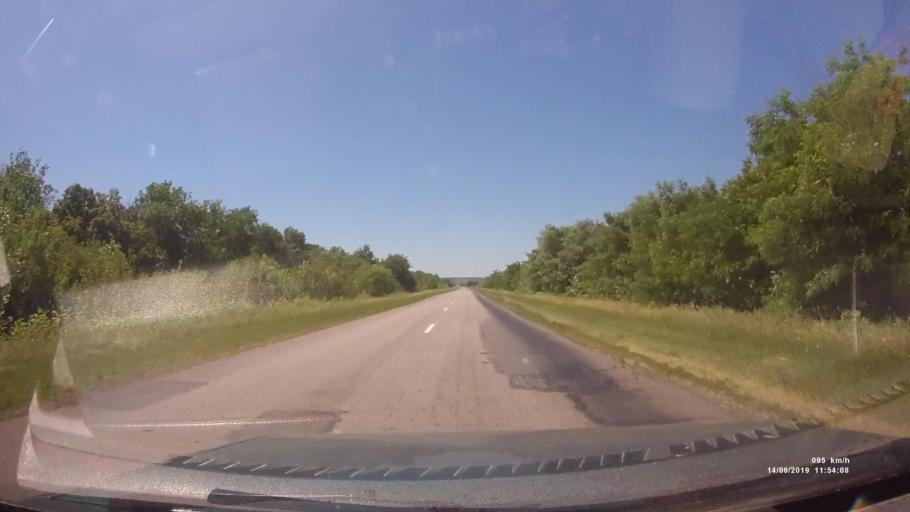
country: RU
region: Rostov
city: Kazanskaya
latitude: 49.8215
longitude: 41.1998
